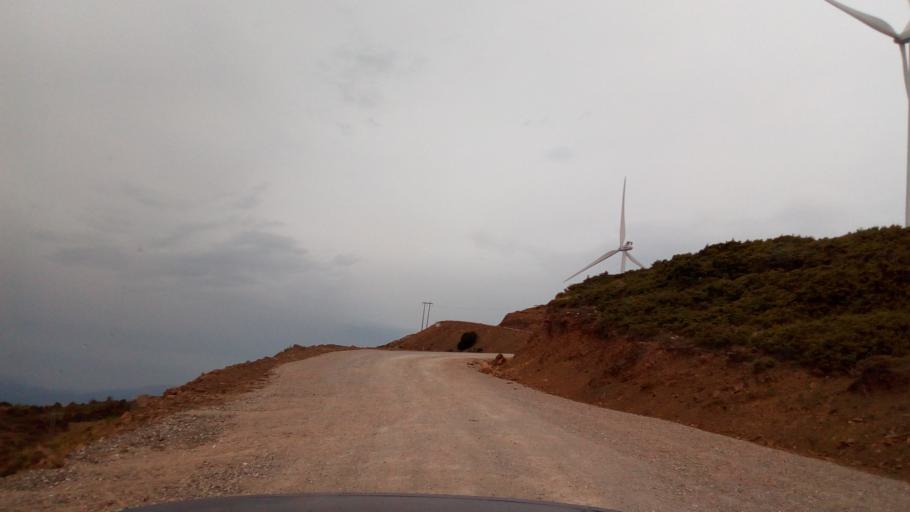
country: GR
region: Central Greece
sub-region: Nomos Fokidos
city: Lidoriki
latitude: 38.4558
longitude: 22.0767
